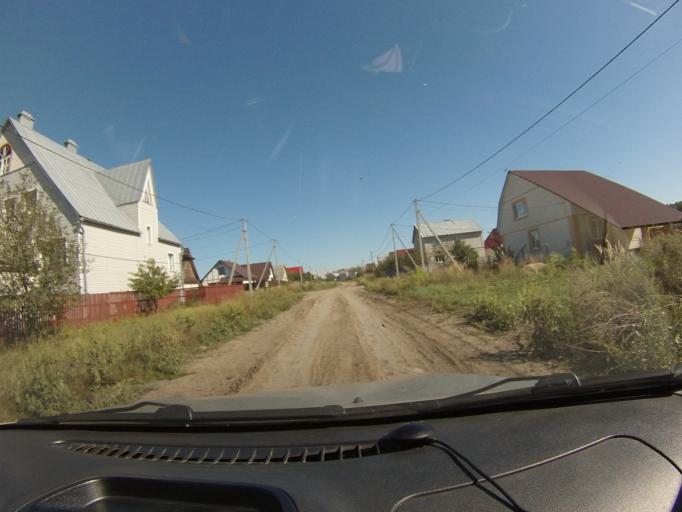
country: RU
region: Tambov
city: Komsomolets
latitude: 52.7606
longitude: 41.3665
